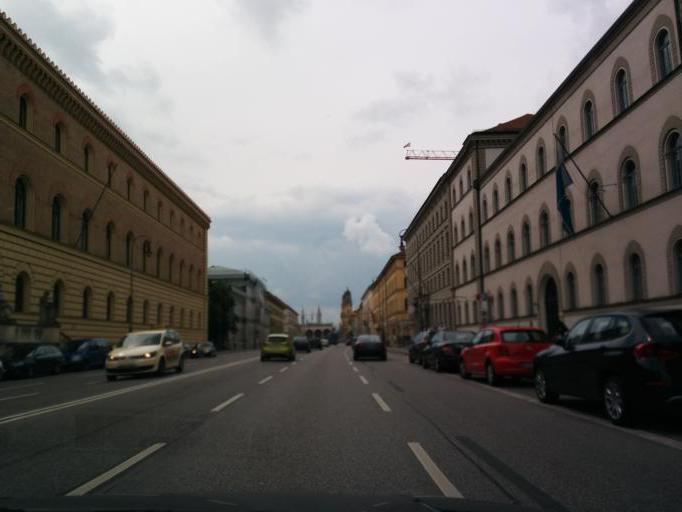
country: DE
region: Bavaria
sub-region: Upper Bavaria
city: Munich
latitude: 48.1478
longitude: 11.5800
